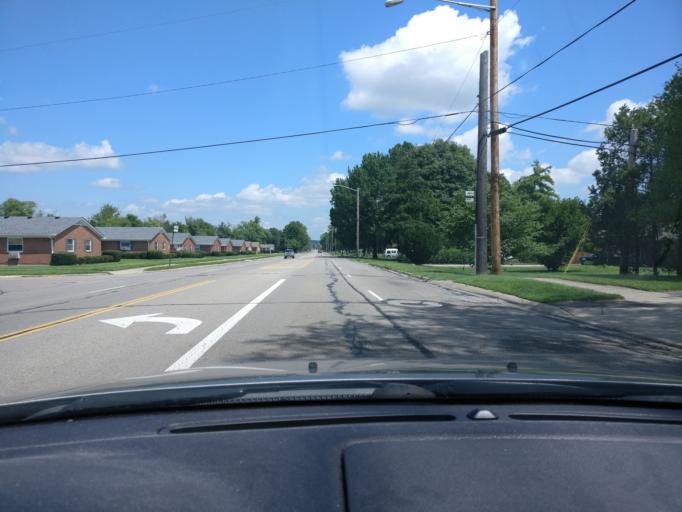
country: US
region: Ohio
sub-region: Montgomery County
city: West Carrollton City
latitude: 39.6610
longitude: -84.2418
